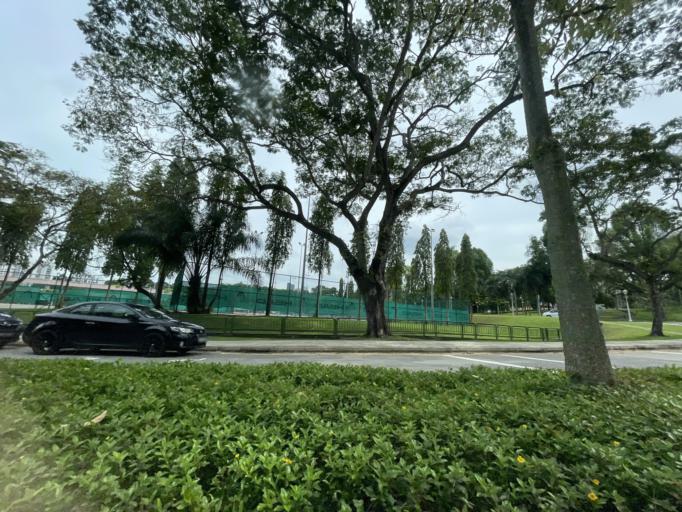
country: SG
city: Singapore
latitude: 1.3207
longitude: 103.8186
